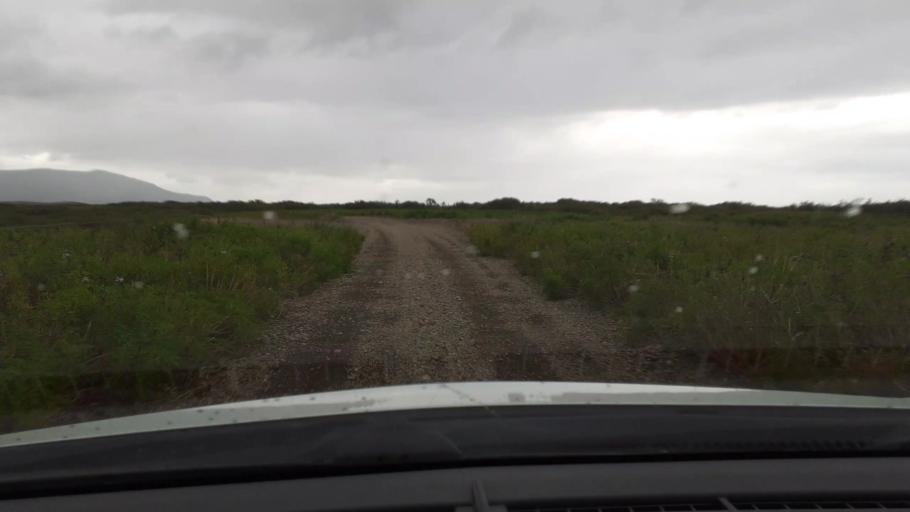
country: IS
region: West
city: Borgarnes
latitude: 64.4570
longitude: -21.9515
